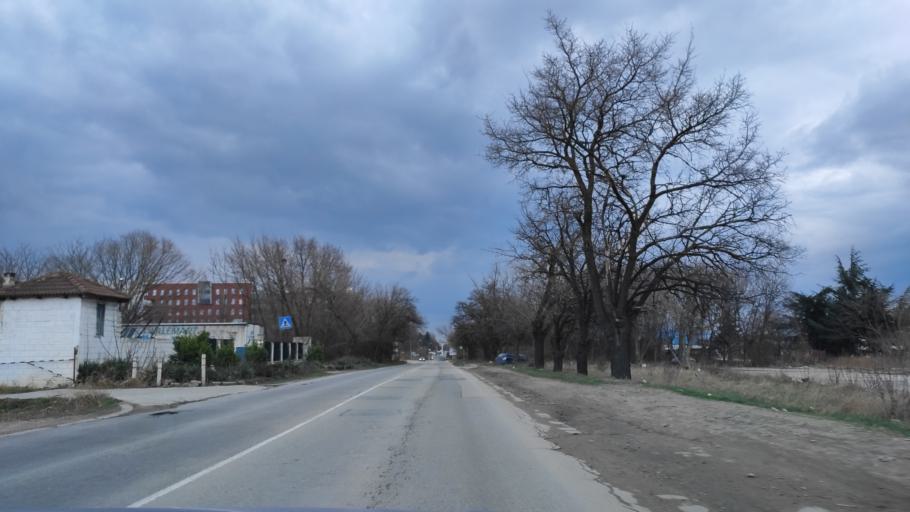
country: BG
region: Varna
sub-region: Obshtina Aksakovo
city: Aksakovo
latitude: 43.2271
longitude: 27.8540
